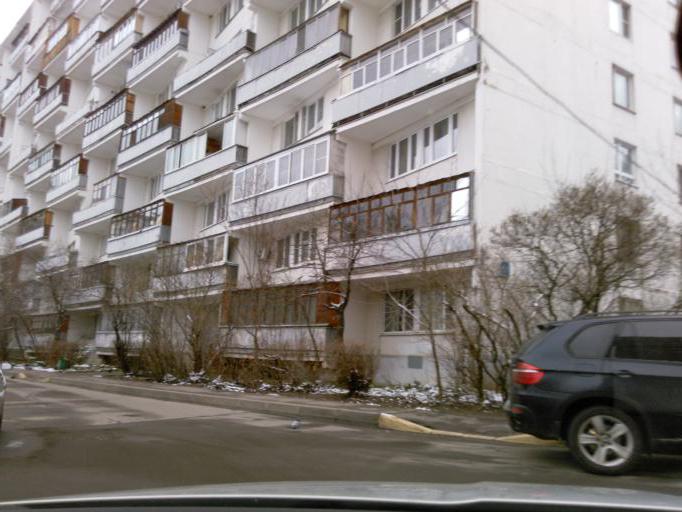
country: RU
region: Moskovskaya
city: Mendeleyevo
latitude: 56.0107
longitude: 37.2090
